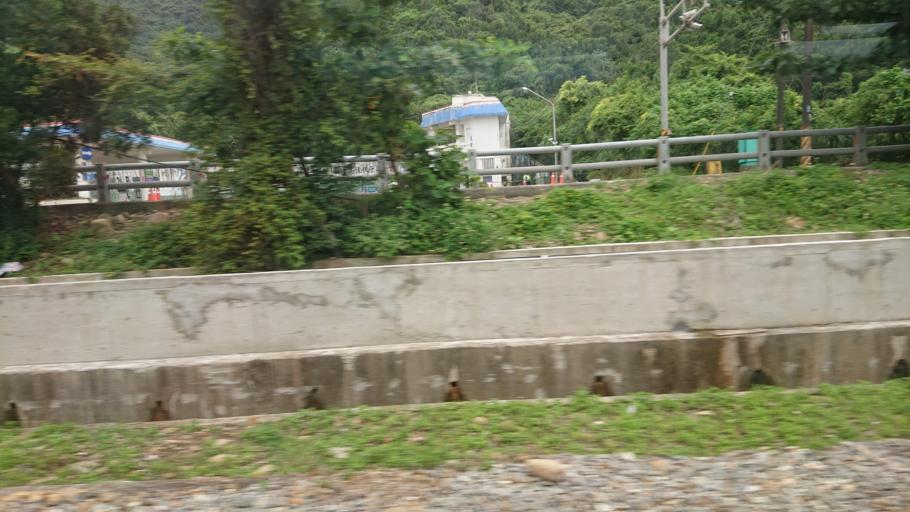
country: TW
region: Taiwan
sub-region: Keelung
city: Keelung
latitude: 24.9714
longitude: 121.9285
